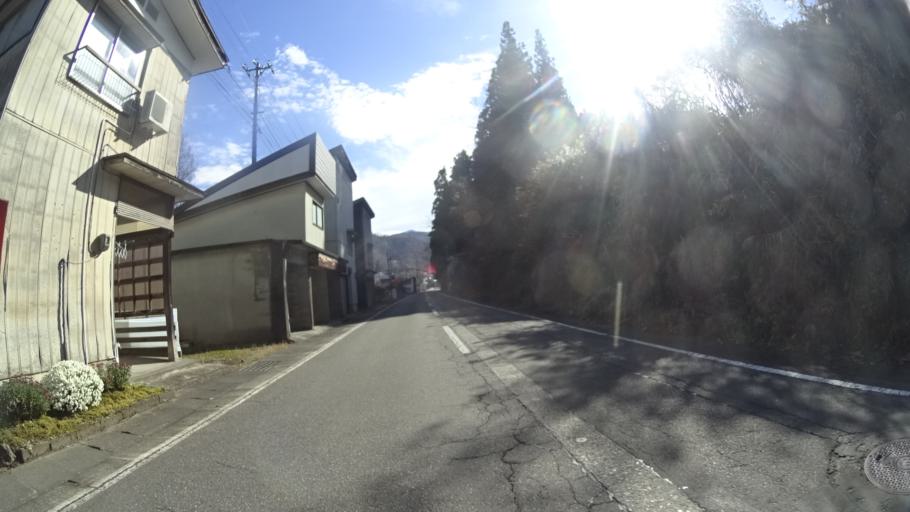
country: JP
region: Niigata
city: Muikamachi
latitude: 37.1958
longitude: 139.0777
